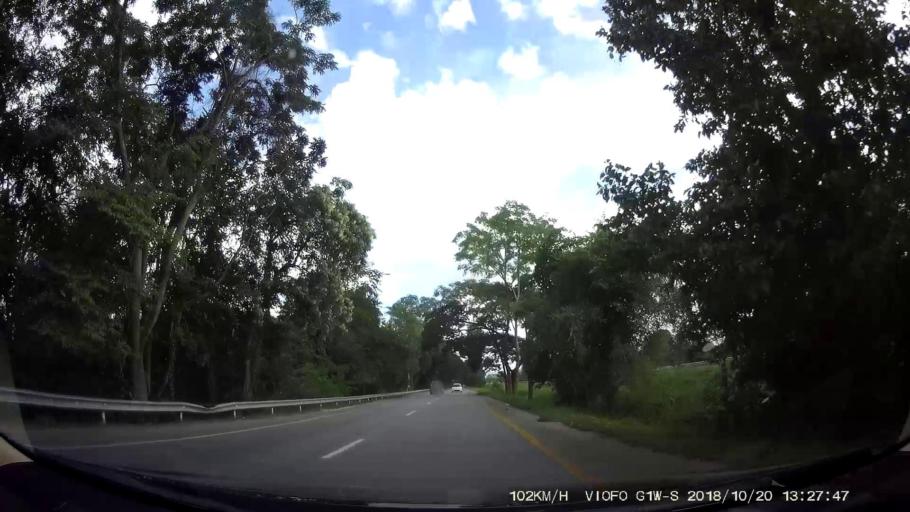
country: TH
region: Chaiyaphum
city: Khon San
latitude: 16.5921
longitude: 101.9660
